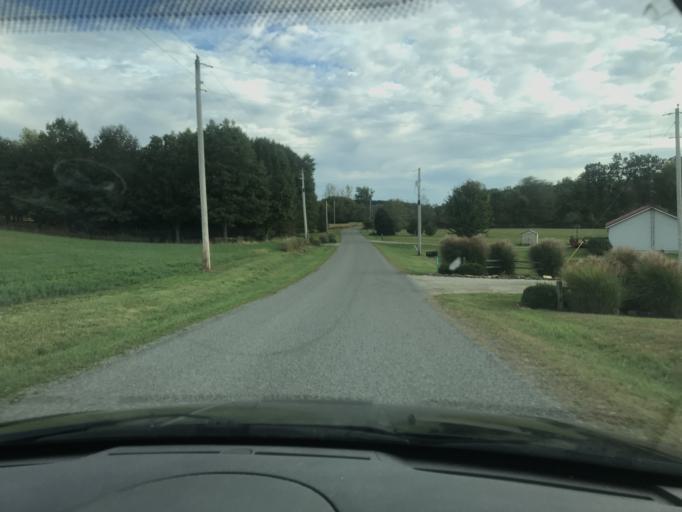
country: US
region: Ohio
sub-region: Logan County
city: West Liberty
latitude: 40.2566
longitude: -83.6977
